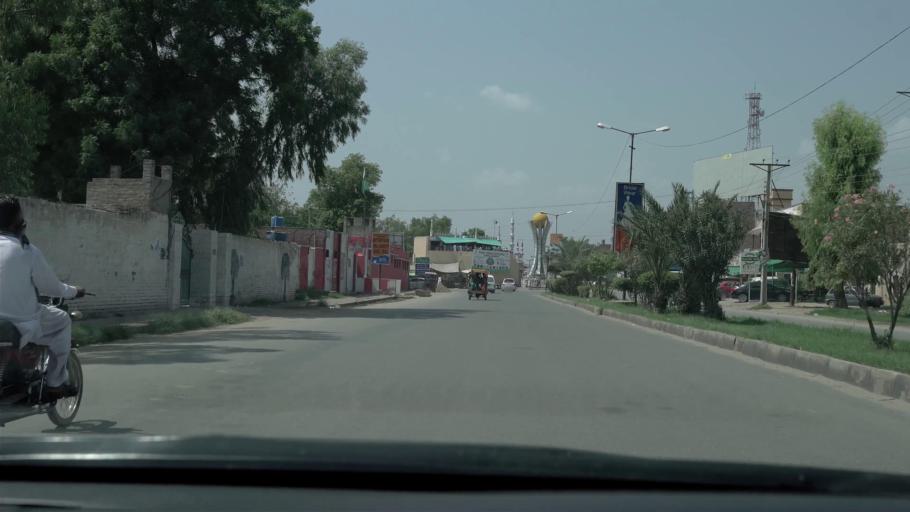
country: PK
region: Punjab
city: Gojra
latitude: 31.1543
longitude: 72.6694
